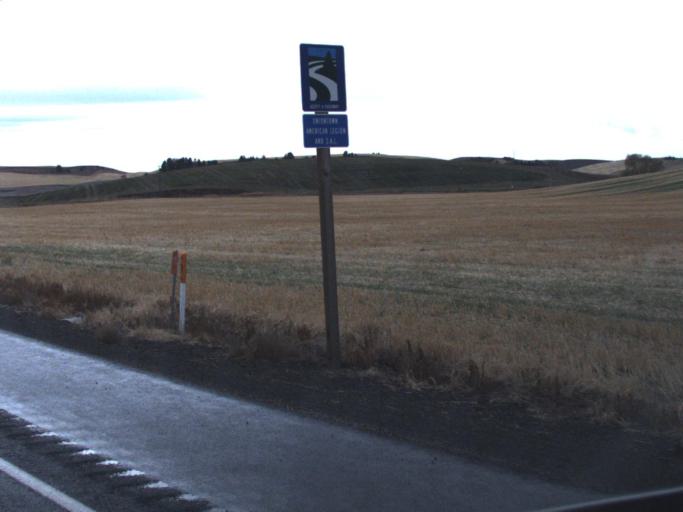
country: US
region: Washington
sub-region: Asotin County
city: Clarkston
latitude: 46.5308
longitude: -117.0852
